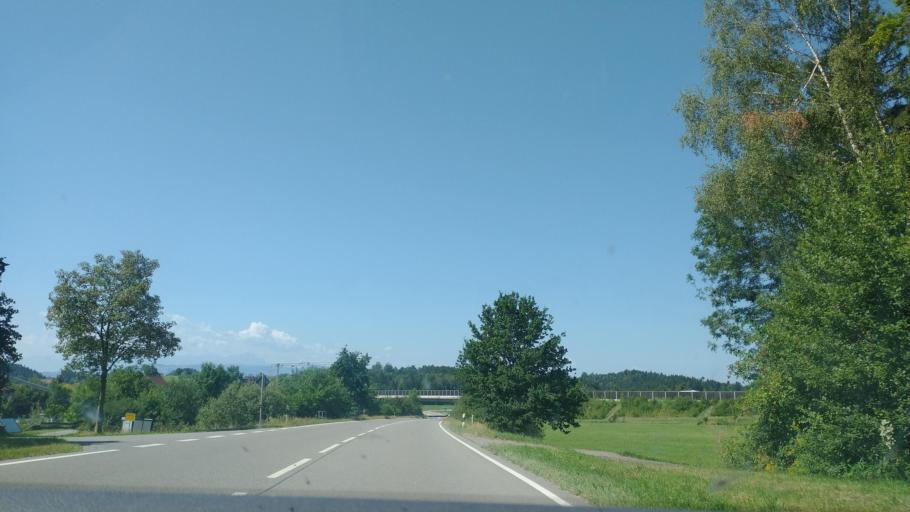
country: DE
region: Bavaria
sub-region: Swabia
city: Weissensberg
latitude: 47.6060
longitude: 9.7356
